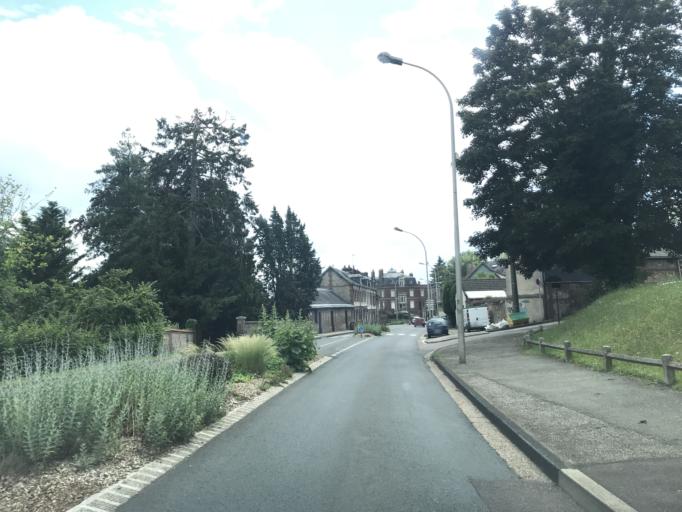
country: FR
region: Haute-Normandie
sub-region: Departement de la Seine-Maritime
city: Mont-Saint-Aignan
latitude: 49.4573
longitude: 1.0826
